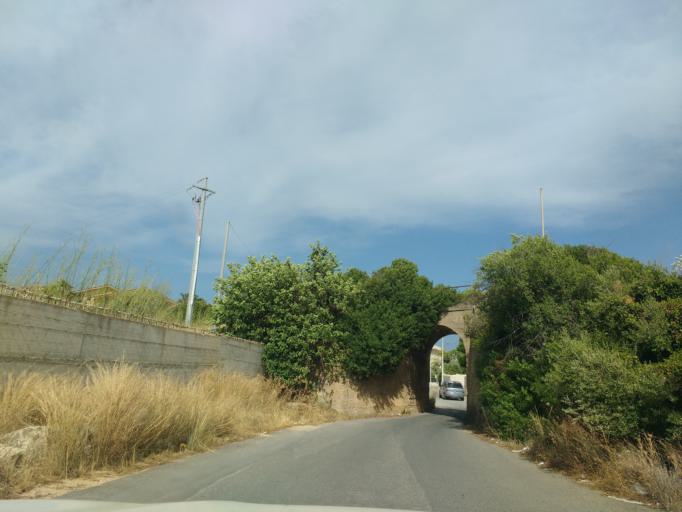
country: IT
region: Sicily
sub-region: Provincia di Siracusa
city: Noto
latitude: 36.8508
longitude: 15.1063
